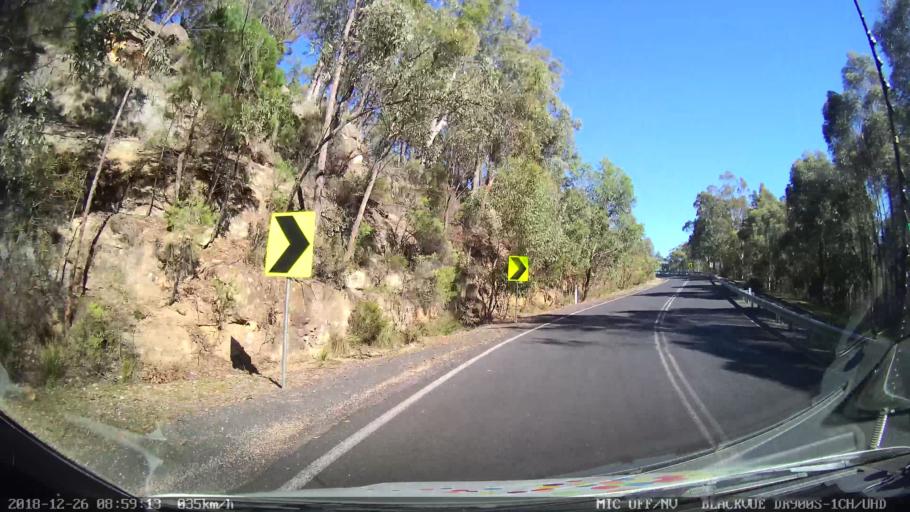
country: AU
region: New South Wales
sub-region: Mid-Western Regional
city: Kandos
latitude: -32.6326
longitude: 150.0397
